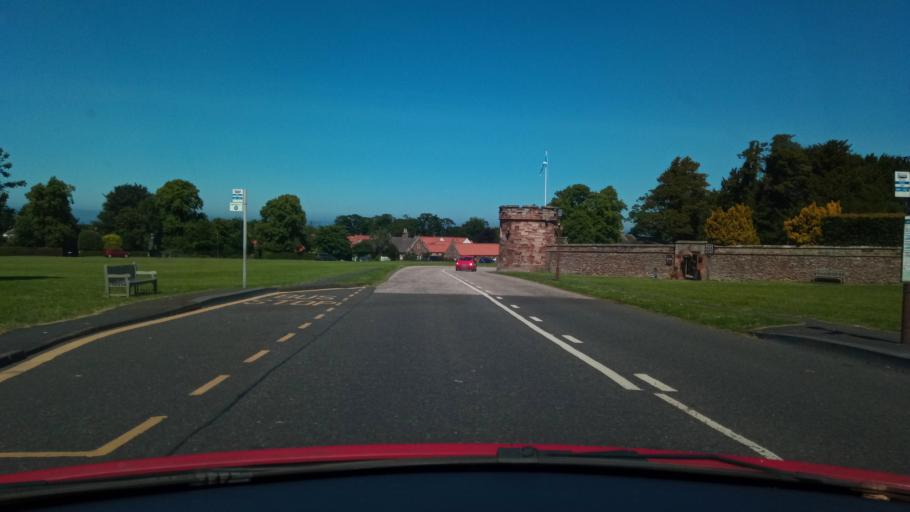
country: GB
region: Scotland
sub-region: East Lothian
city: Gullane
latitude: 56.0457
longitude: -2.7814
